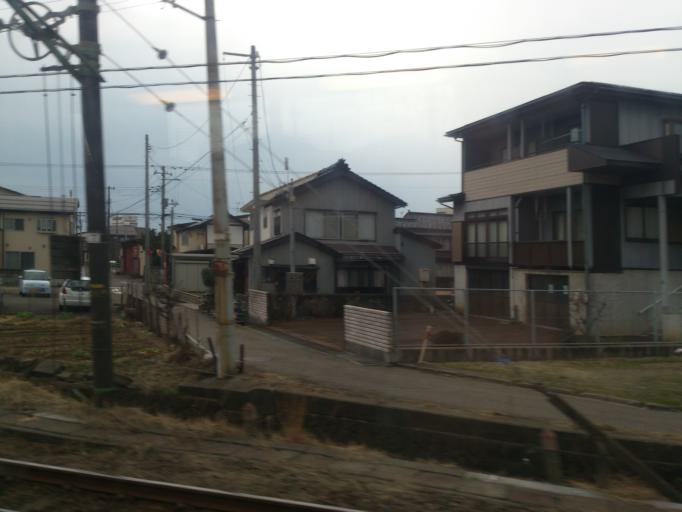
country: JP
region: Niigata
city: Joetsu
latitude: 37.1689
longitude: 138.2397
